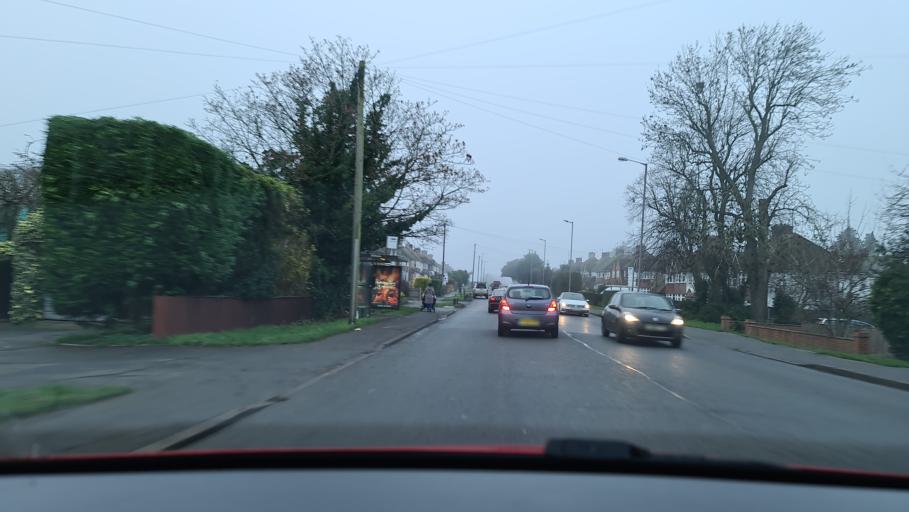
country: GB
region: England
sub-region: Buckinghamshire
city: Weston Turville
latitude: 51.8124
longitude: -0.7794
